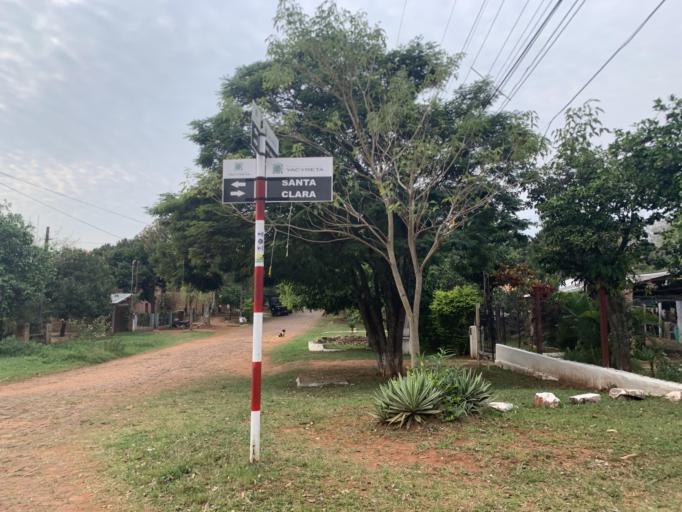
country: PY
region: Misiones
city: San Juan Bautista
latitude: -26.6651
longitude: -57.1524
